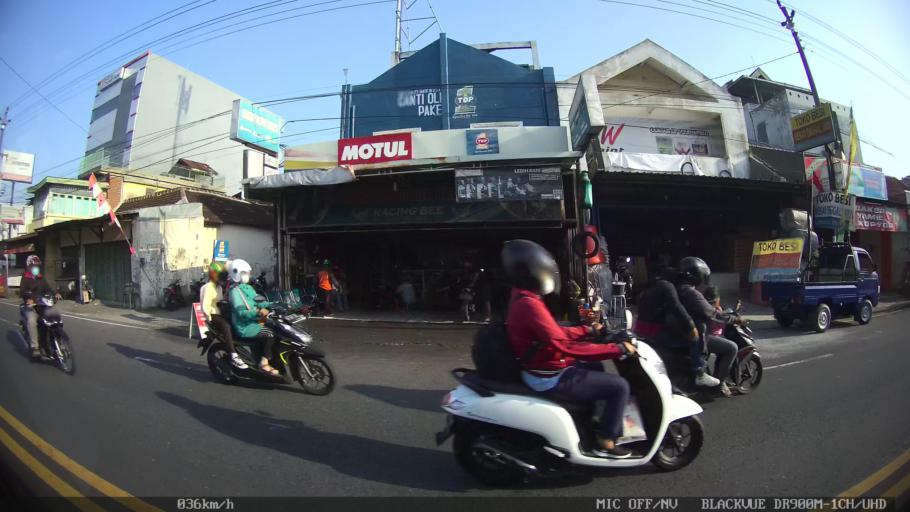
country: ID
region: Daerah Istimewa Yogyakarta
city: Gamping Lor
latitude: -7.8013
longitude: 110.3474
